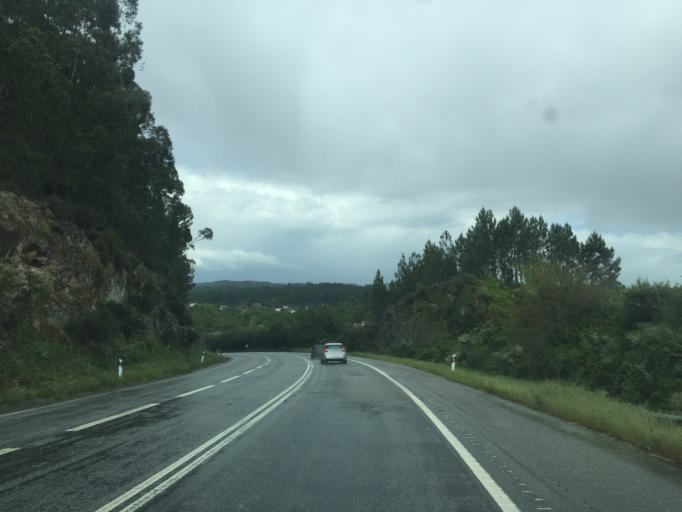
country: PT
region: Viseu
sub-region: Viseu
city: Abraveses
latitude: 40.6606
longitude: -8.0063
